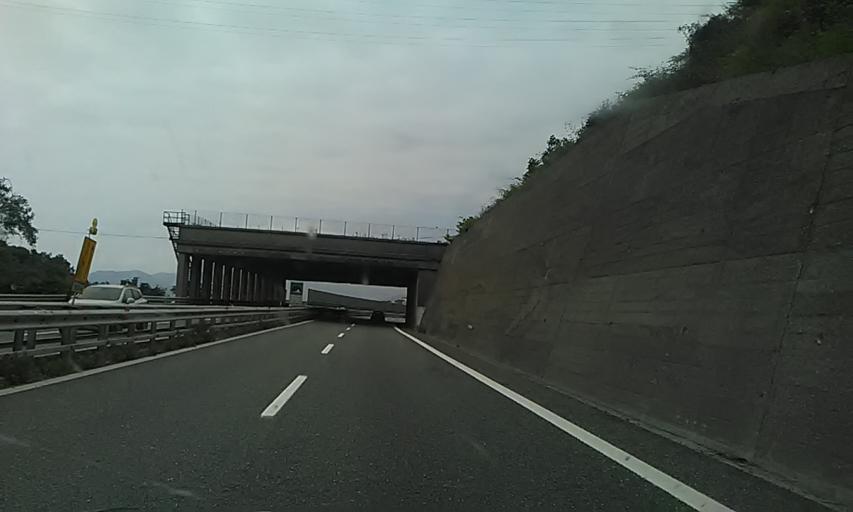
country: IT
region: Liguria
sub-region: Provincia di Savona
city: Savona
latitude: 44.3204
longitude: 8.4813
